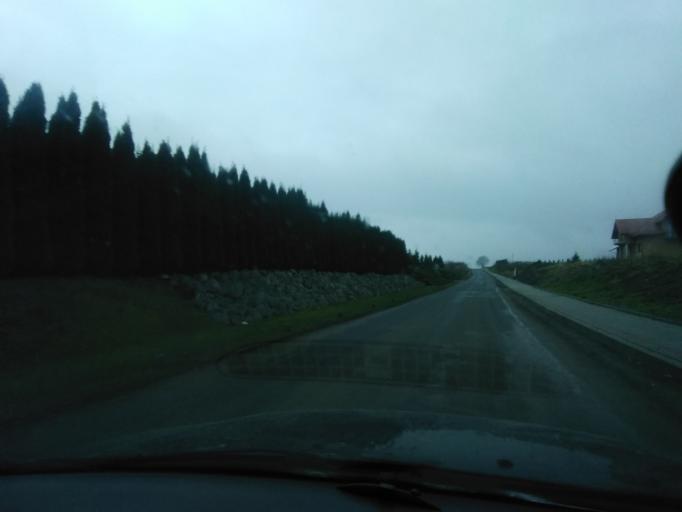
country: PL
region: Subcarpathian Voivodeship
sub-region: Powiat jaroslawski
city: Rokietnica
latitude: 49.9148
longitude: 22.6128
